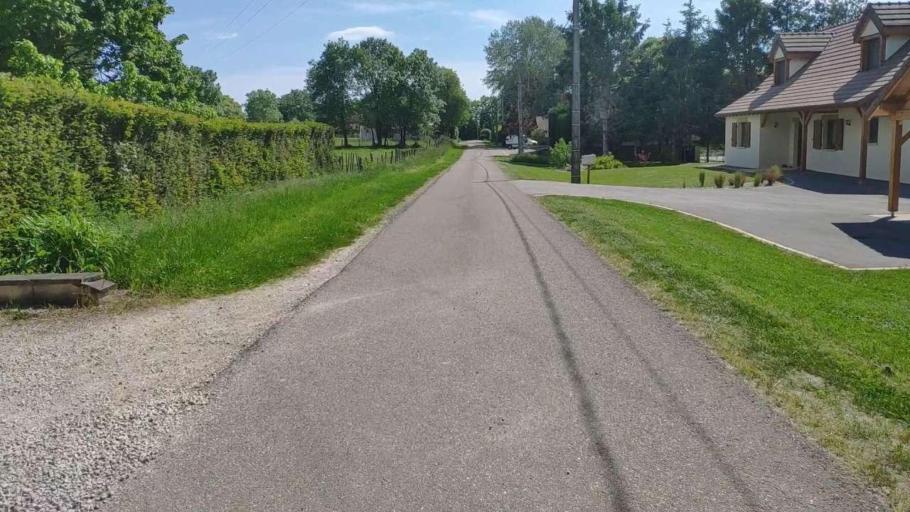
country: FR
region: Franche-Comte
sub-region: Departement du Jura
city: Bletterans
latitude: 46.8044
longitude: 5.4100
